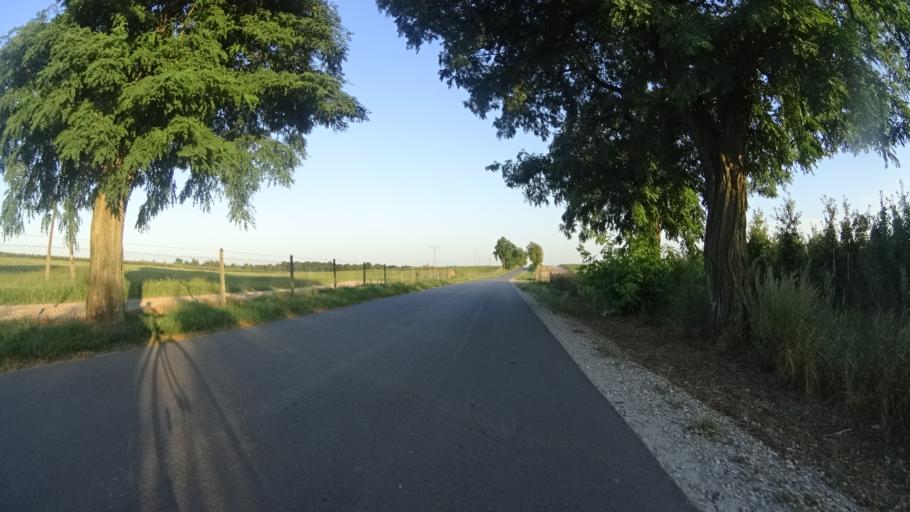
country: PL
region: Masovian Voivodeship
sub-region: Powiat grojecki
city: Goszczyn
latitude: 51.6844
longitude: 20.8232
